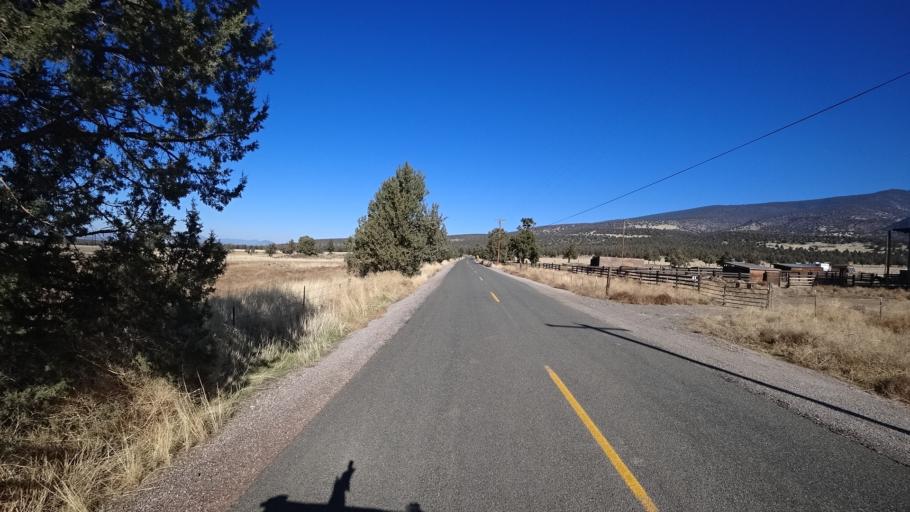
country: US
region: California
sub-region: Siskiyou County
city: Weed
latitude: 41.5976
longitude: -122.3019
